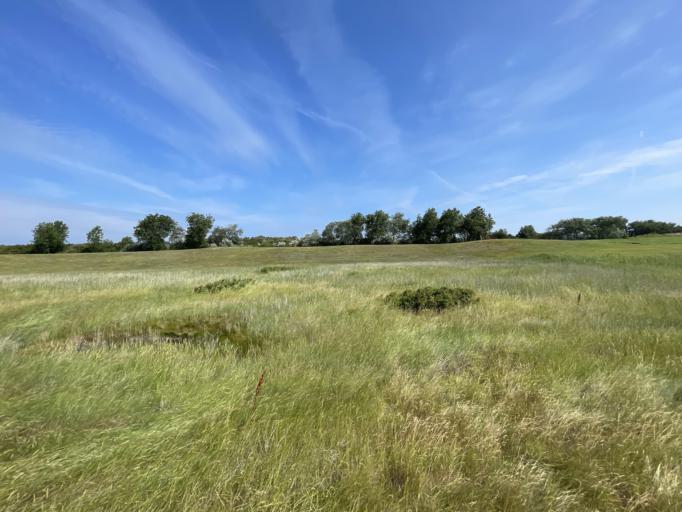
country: DE
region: Lower Saxony
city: Wangerooge
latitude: 53.7876
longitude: 7.8901
